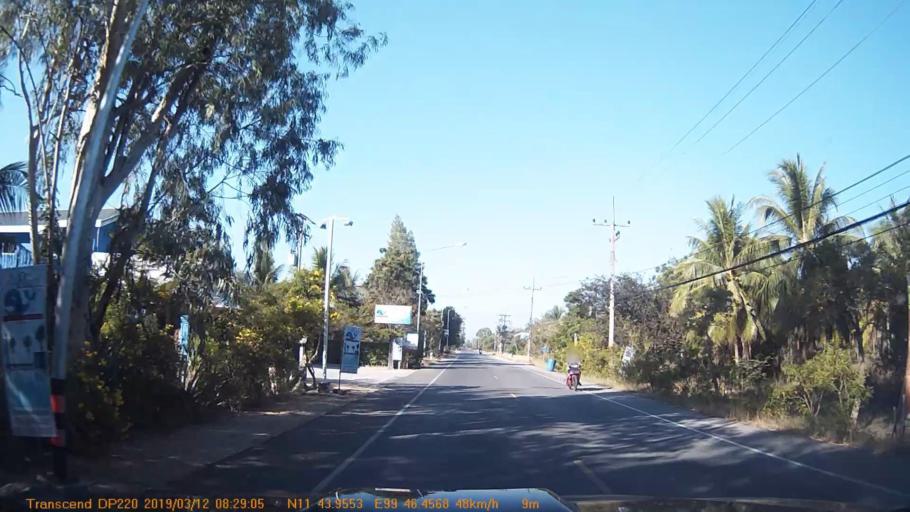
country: TH
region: Prachuap Khiri Khan
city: Prachuap Khiri Khan
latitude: 11.7325
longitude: 99.7742
